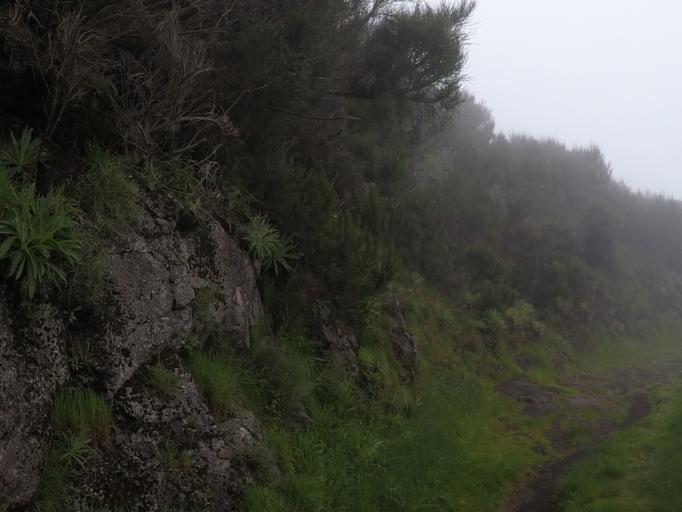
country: PT
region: Madeira
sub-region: Camara de Lobos
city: Curral das Freiras
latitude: 32.7248
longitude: -16.9867
